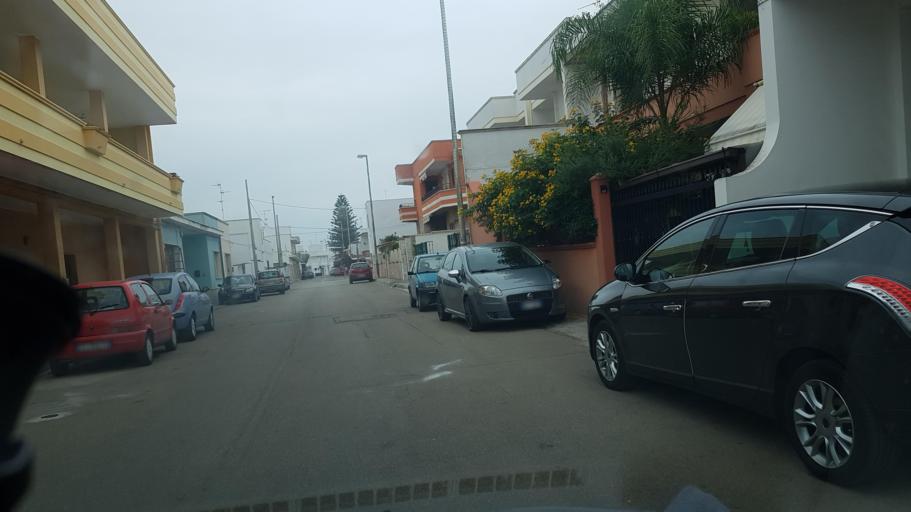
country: IT
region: Apulia
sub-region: Provincia di Lecce
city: Veglie
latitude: 40.3355
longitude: 17.9587
